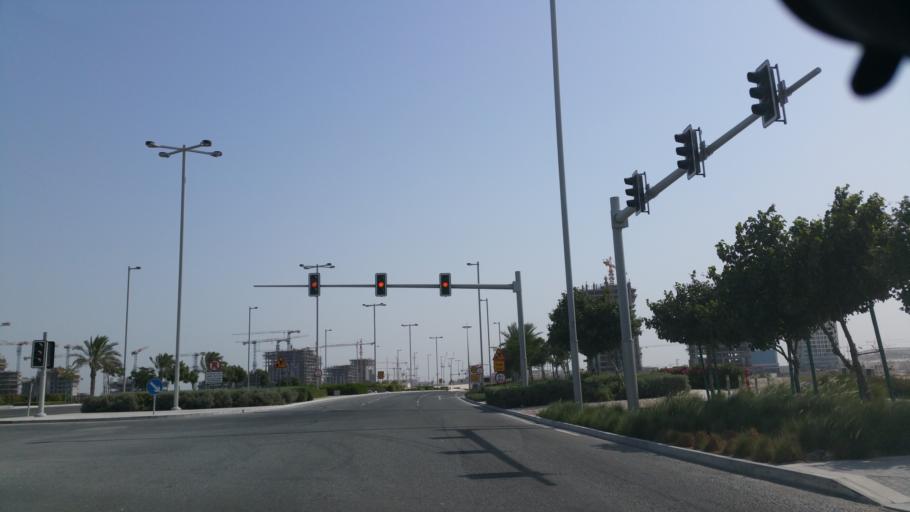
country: QA
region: Baladiyat Umm Salal
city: Umm Salal Muhammad
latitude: 25.4335
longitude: 51.5145
